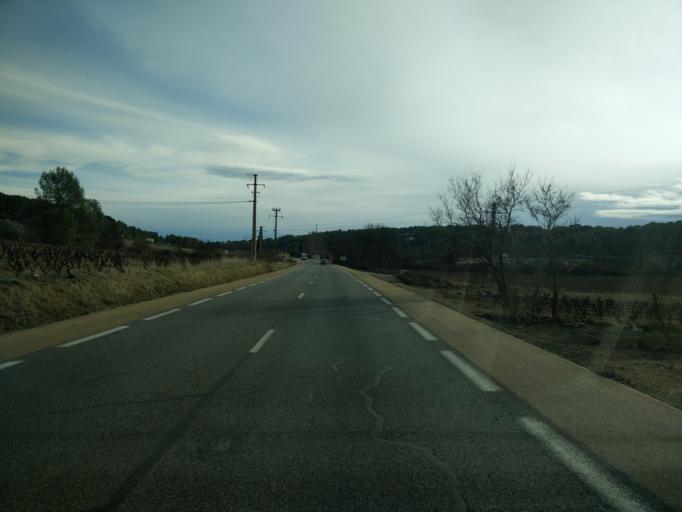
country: FR
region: Provence-Alpes-Cote d'Azur
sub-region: Departement du Var
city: Lorgues
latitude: 43.4798
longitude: 6.3717
